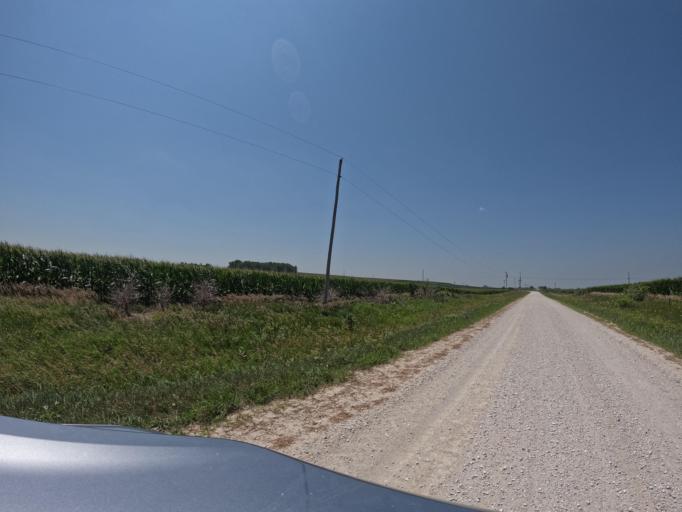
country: US
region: Iowa
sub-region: Keokuk County
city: Sigourney
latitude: 41.2868
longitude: -92.1778
